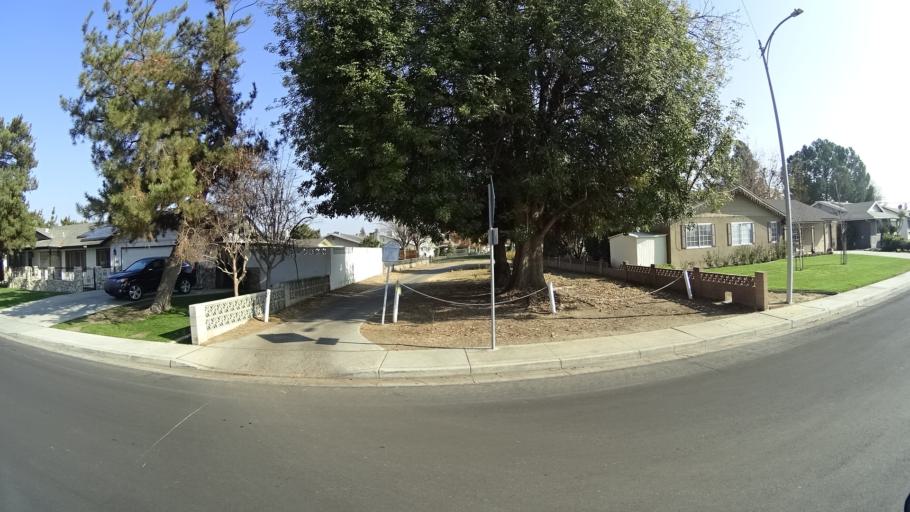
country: US
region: California
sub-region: Kern County
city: Greenacres
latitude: 35.3529
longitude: -119.0672
